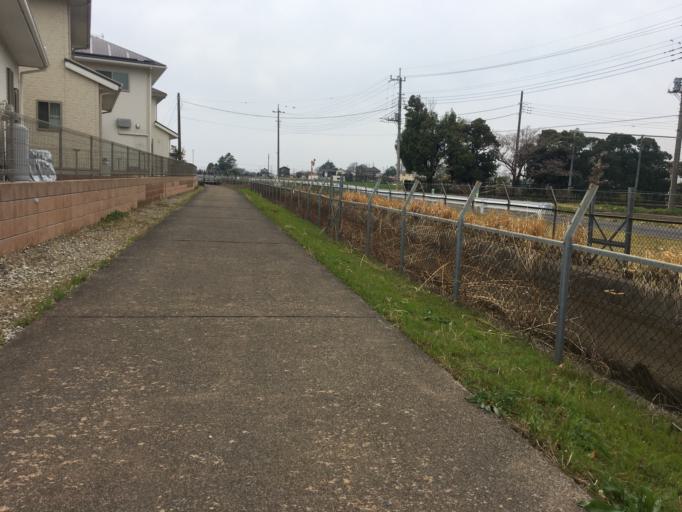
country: JP
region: Saitama
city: Kisai
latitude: 36.1134
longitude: 139.5822
